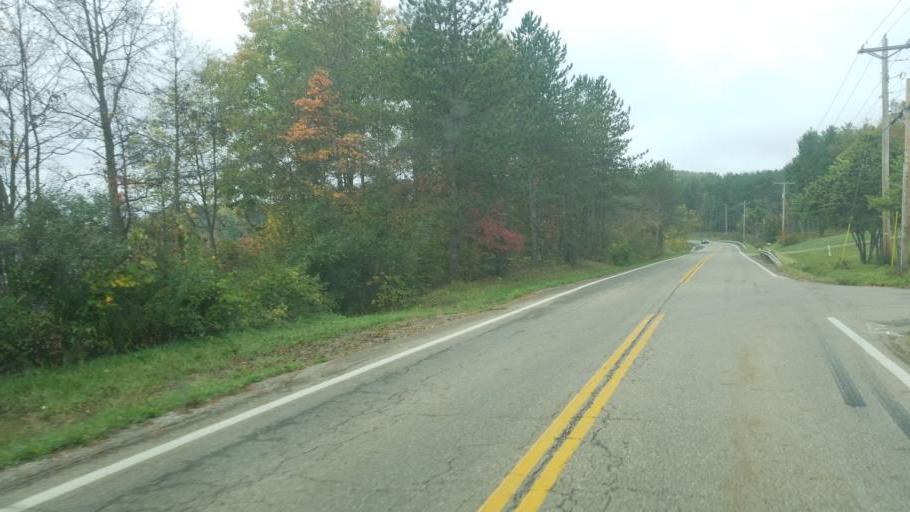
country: US
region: Ohio
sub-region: Tuscarawas County
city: Rockford
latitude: 40.5581
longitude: -81.2300
